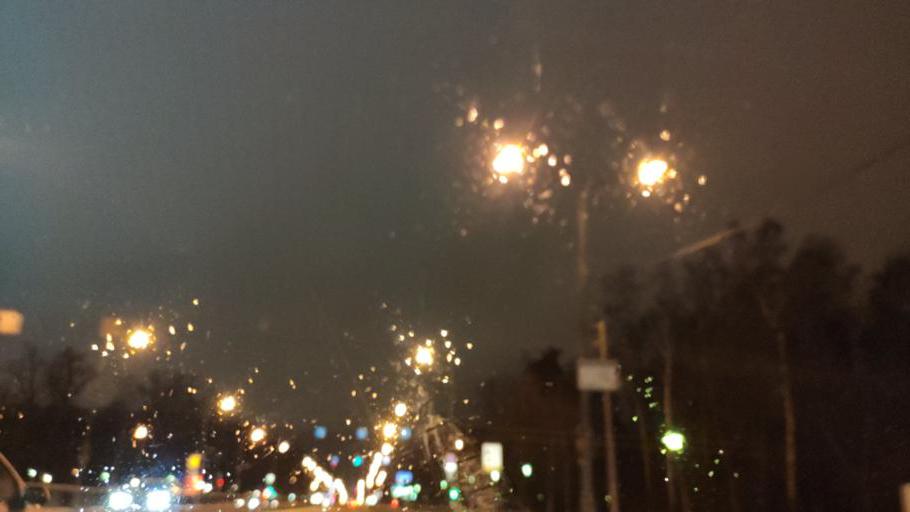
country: RU
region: Moskovskaya
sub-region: Leninskiy Rayon
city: Vnukovo
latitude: 55.6057
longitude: 37.2973
